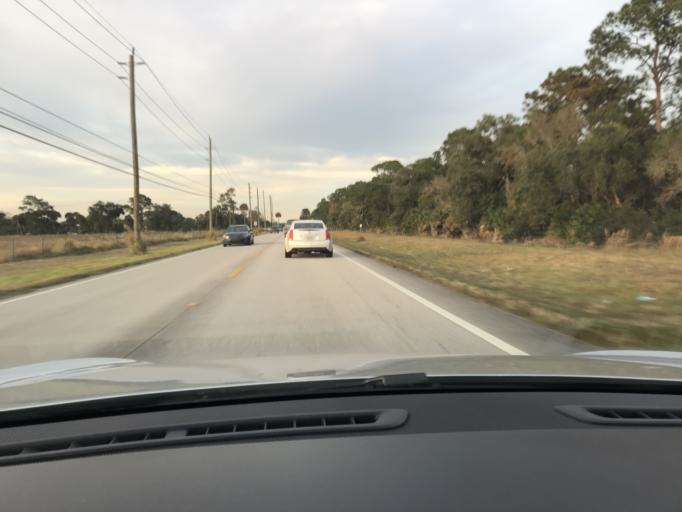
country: US
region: Florida
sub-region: Indian River County
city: Vero Beach South
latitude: 27.5774
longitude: -80.4307
